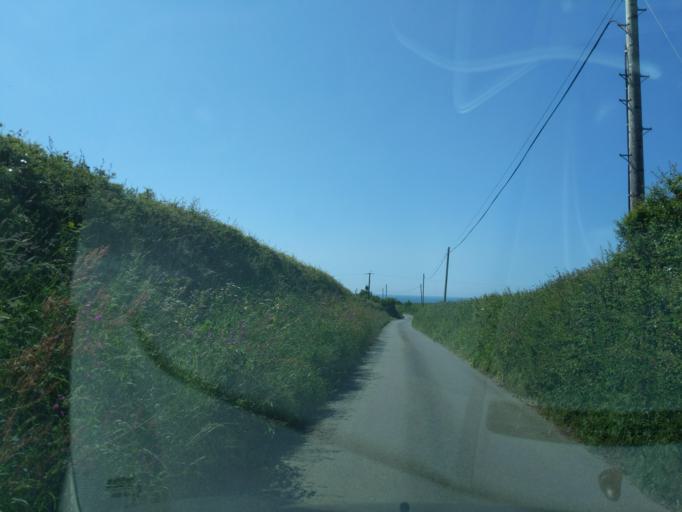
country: GB
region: England
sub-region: Cornwall
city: Wadebridge
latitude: 50.5835
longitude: -4.8437
